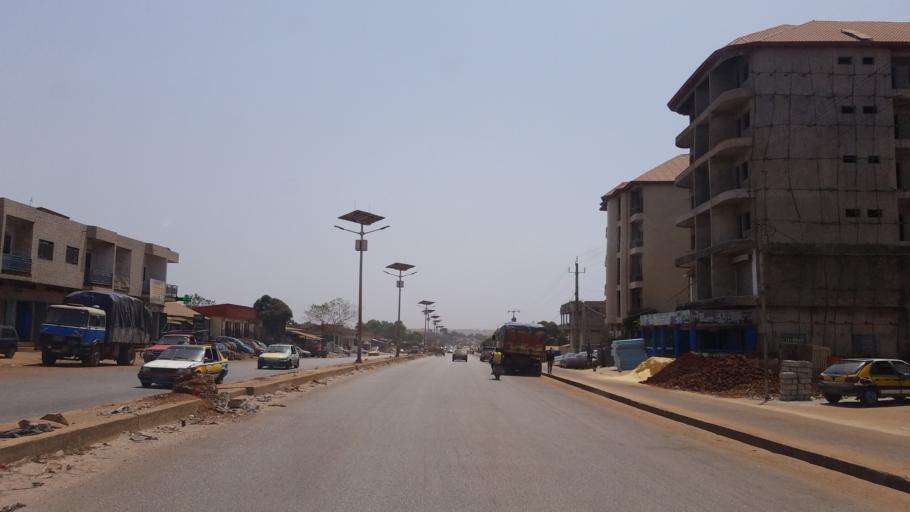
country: GN
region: Kindia
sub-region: Prefecture de Dubreka
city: Dubreka
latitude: 9.6624
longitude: -13.5641
